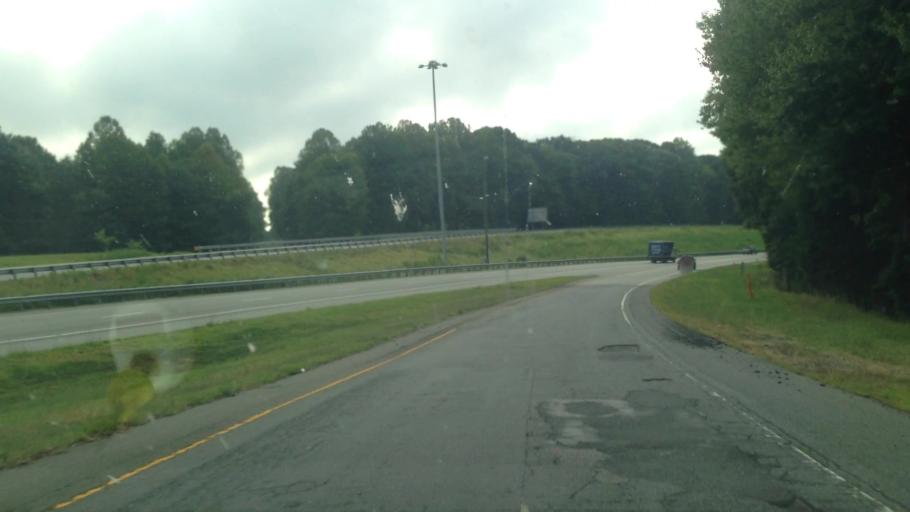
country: US
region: North Carolina
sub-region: Forsyth County
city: Kernersville
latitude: 36.1123
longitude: -80.0615
